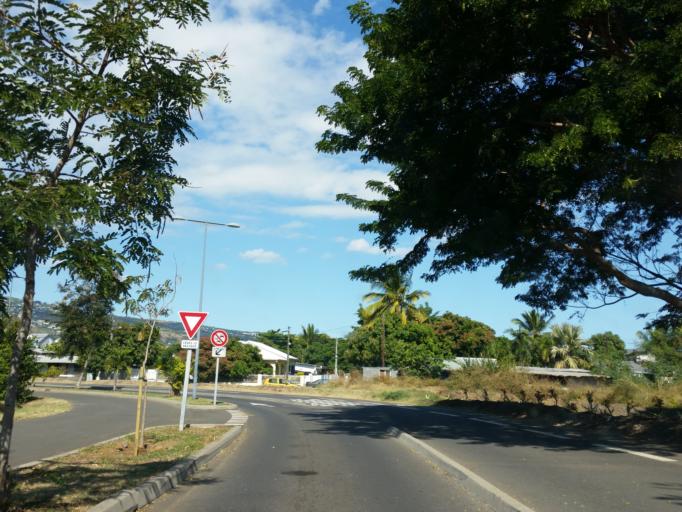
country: RE
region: Reunion
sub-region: Reunion
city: Saint-Paul
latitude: -20.9818
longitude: 55.2878
